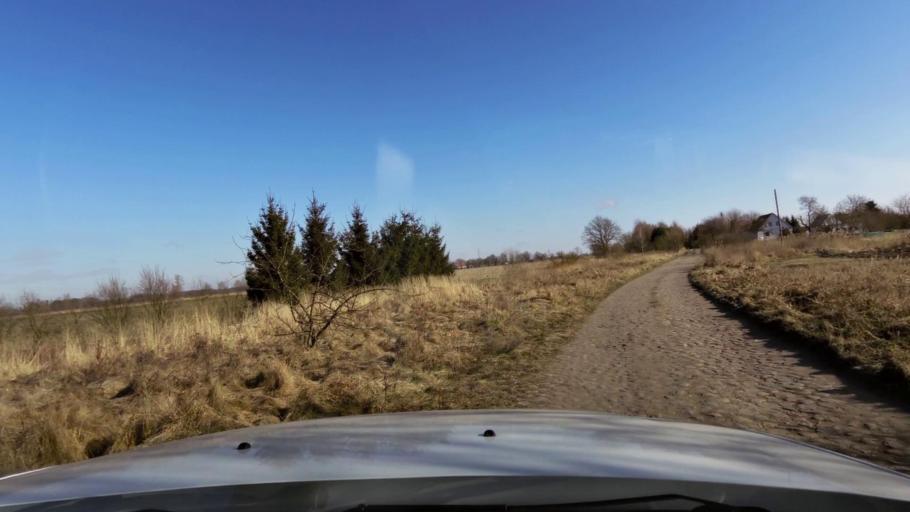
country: PL
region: West Pomeranian Voivodeship
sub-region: Powiat pyrzycki
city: Lipiany
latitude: 52.9684
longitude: 15.0140
